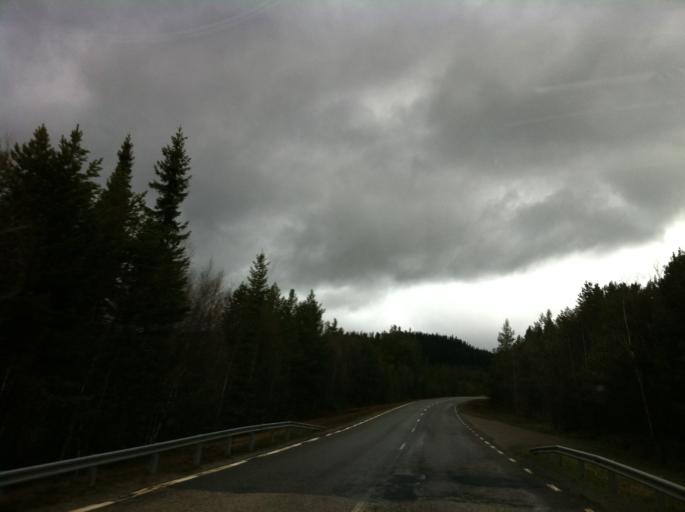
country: NO
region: Hedmark
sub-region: Engerdal
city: Engerdal
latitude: 62.4244
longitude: 12.7404
